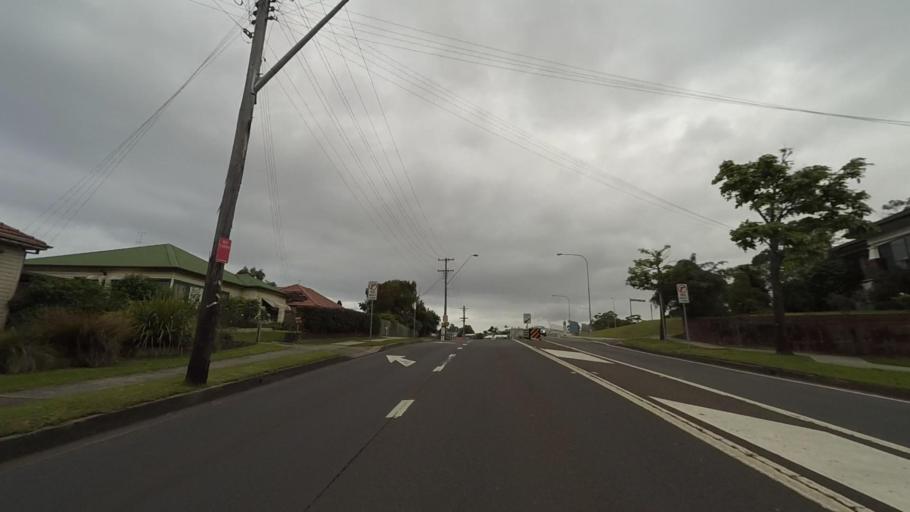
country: AU
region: New South Wales
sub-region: Wollongong
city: Bulli
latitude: -34.3215
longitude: 150.9137
